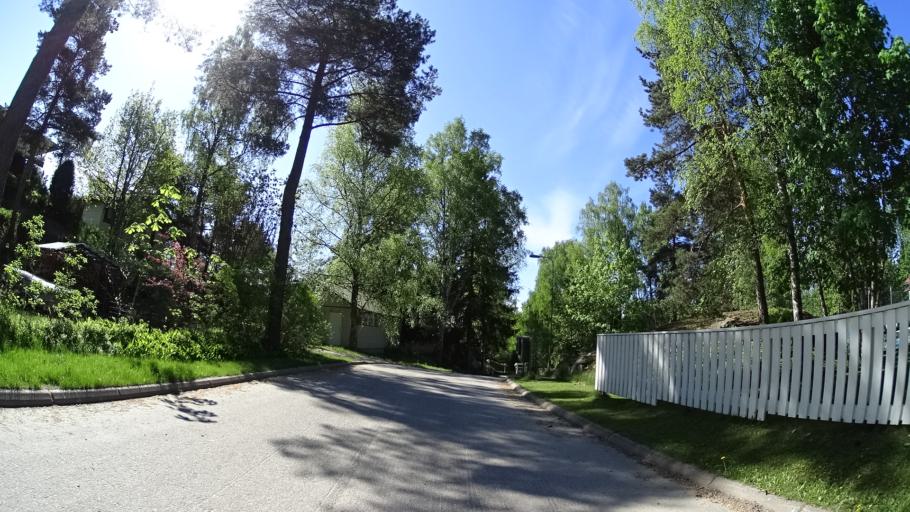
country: FI
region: Uusimaa
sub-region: Helsinki
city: Espoo
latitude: 60.1657
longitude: 24.6762
